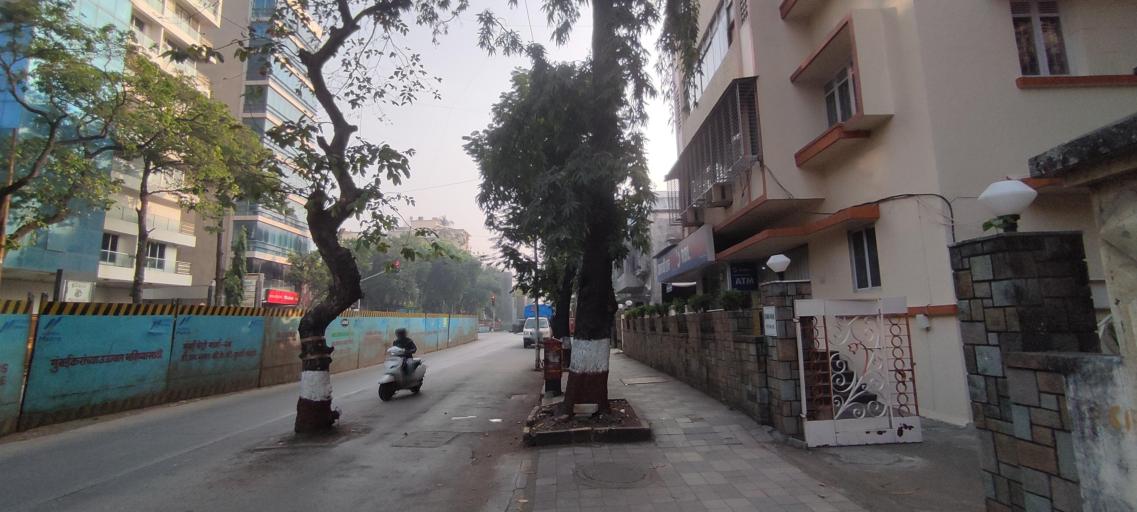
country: IN
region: Maharashtra
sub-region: Mumbai Suburban
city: Mumbai
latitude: 19.0718
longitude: 72.8371
